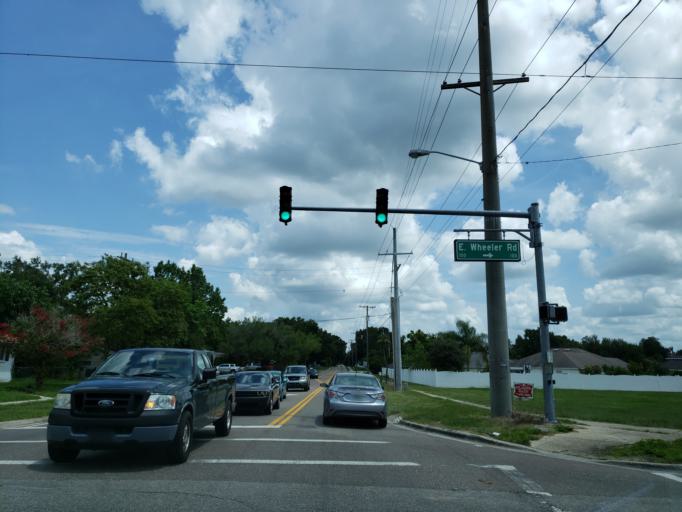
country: US
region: Florida
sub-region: Hillsborough County
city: Seffner
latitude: 27.9743
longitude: -82.2777
